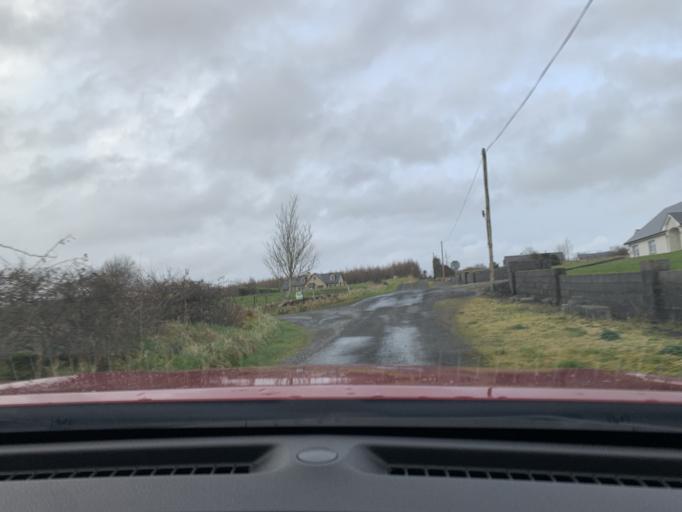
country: IE
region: Connaught
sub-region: Roscommon
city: Boyle
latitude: 53.9822
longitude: -8.4230
